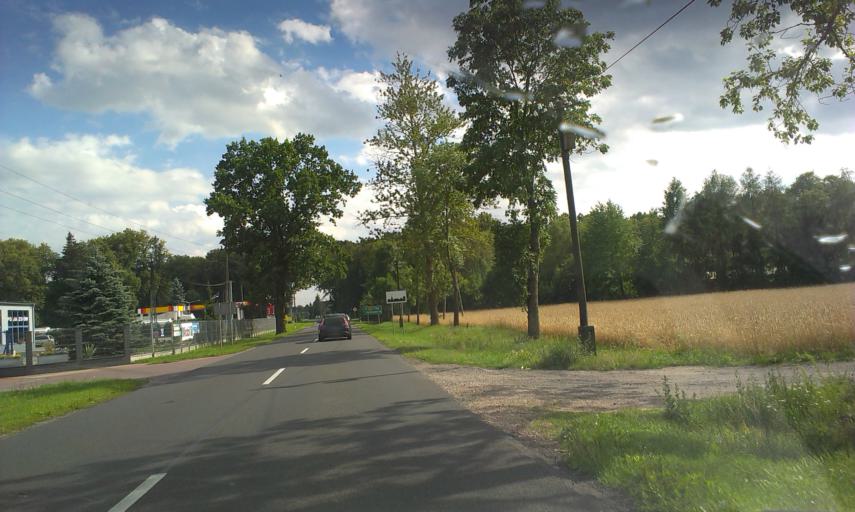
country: PL
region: Greater Poland Voivodeship
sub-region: Powiat zlotowski
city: Krajenka
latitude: 53.3044
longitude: 16.9882
